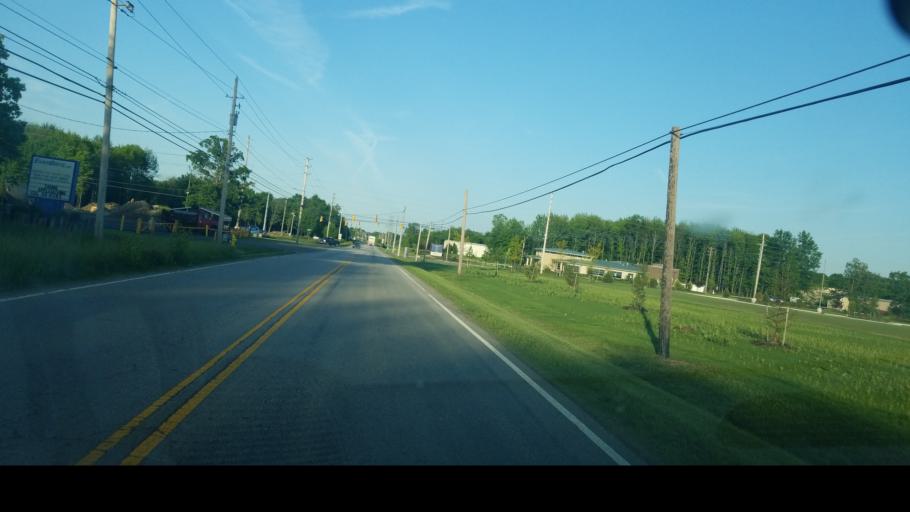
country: US
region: Ohio
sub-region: Trumbull County
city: Lordstown
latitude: 41.0994
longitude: -80.8890
